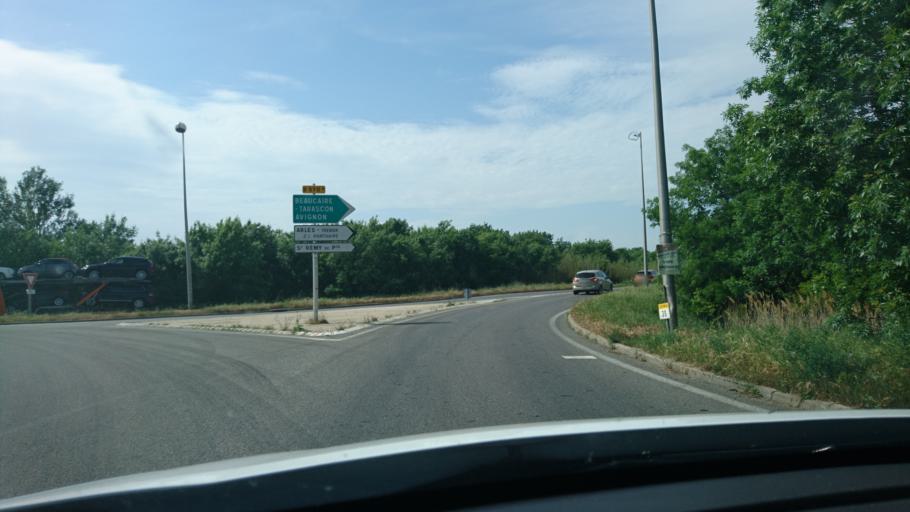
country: FR
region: Provence-Alpes-Cote d'Azur
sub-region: Departement des Bouches-du-Rhone
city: Arles
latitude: 43.6910
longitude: 4.6443
